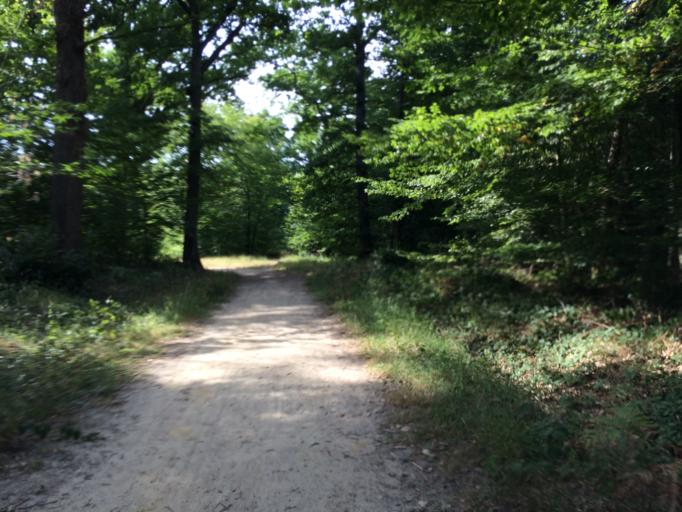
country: FR
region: Ile-de-France
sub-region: Departement de l'Essonne
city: Epinay-sous-Senart
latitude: 48.6788
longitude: 2.5121
